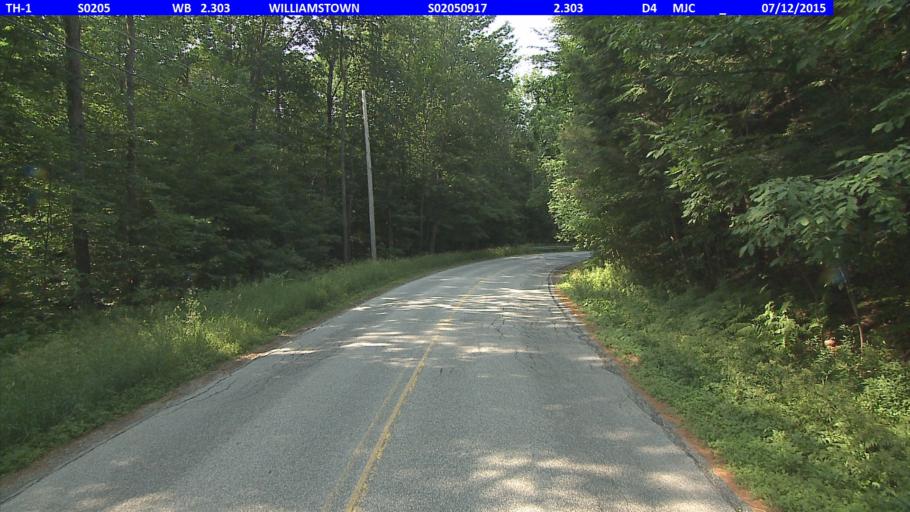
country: US
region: Vermont
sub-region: Orange County
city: Williamstown
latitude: 44.1261
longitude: -72.4992
